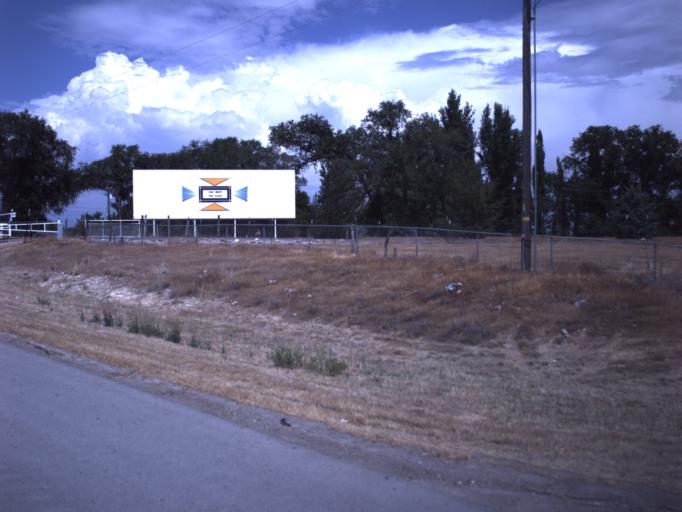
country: US
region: Utah
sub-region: Uintah County
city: Naples
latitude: 40.4118
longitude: -109.4931
